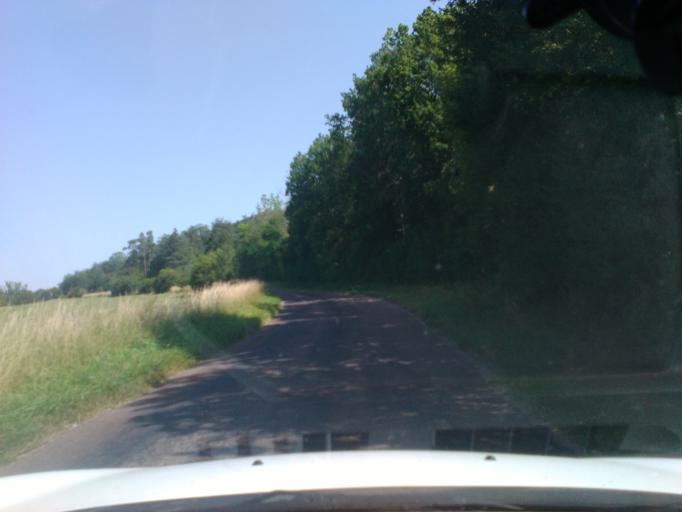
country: FR
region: Lorraine
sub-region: Departement des Vosges
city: Liffol-le-Grand
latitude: 48.2910
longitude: 5.4840
